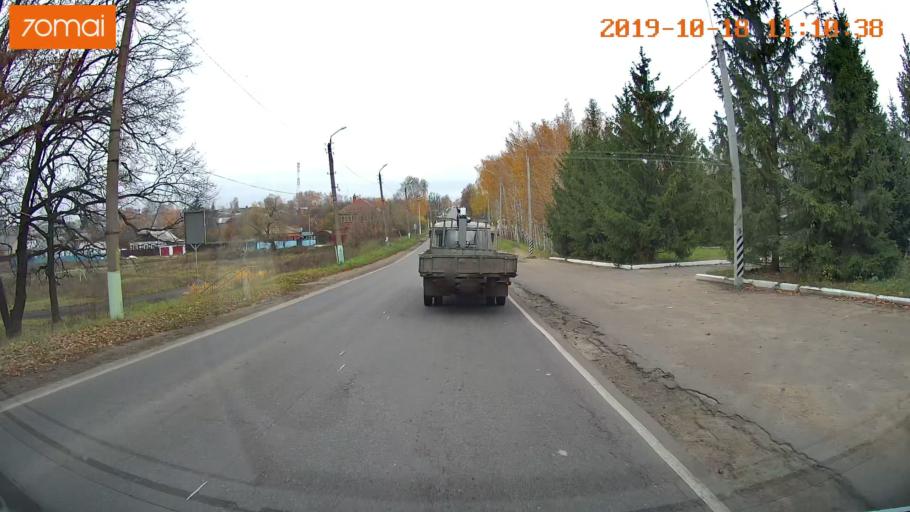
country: RU
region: Tula
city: Kimovsk
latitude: 53.9569
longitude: 38.5385
